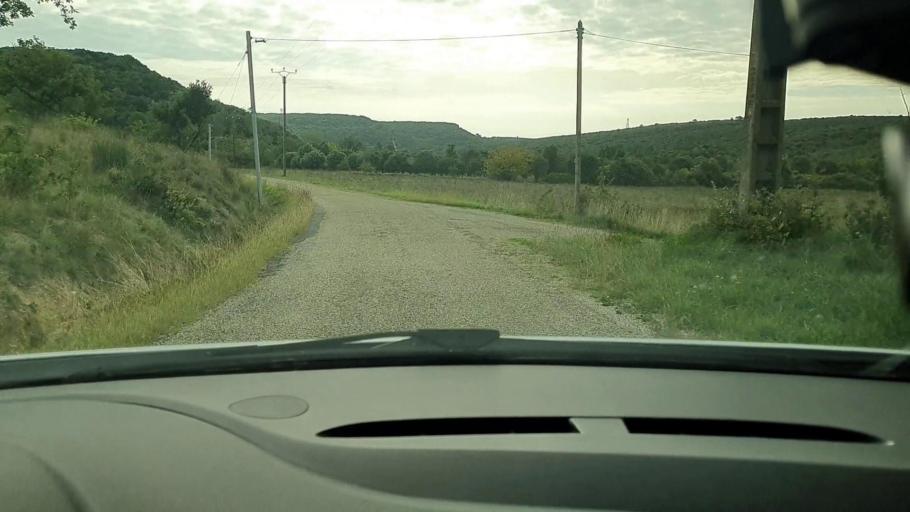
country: FR
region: Languedoc-Roussillon
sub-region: Departement du Gard
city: Montaren-et-Saint-Mediers
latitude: 44.1052
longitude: 4.3052
